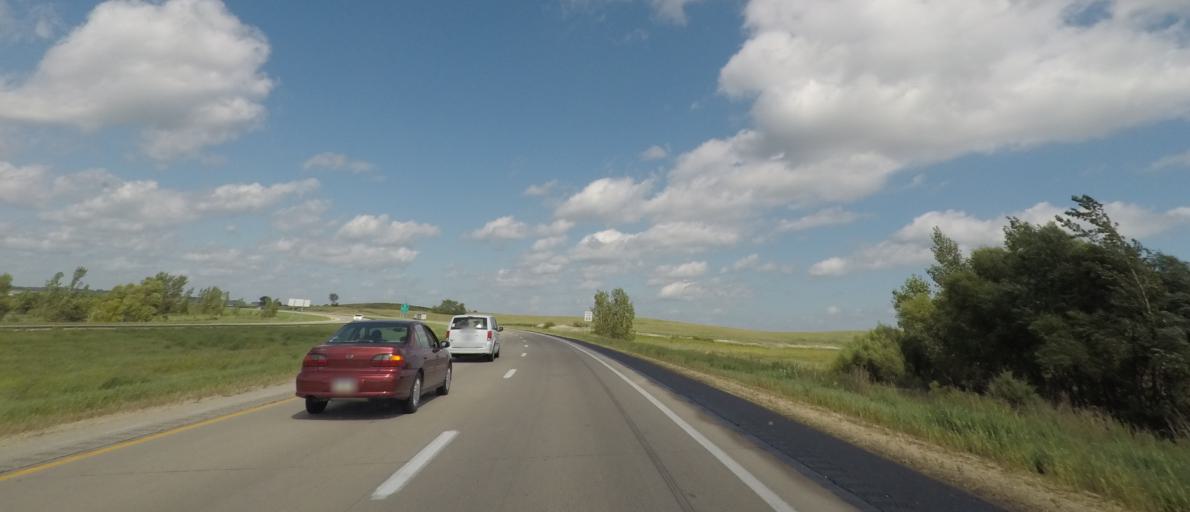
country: US
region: Iowa
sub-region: Jones County
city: Monticello
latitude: 42.2088
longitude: -91.1772
